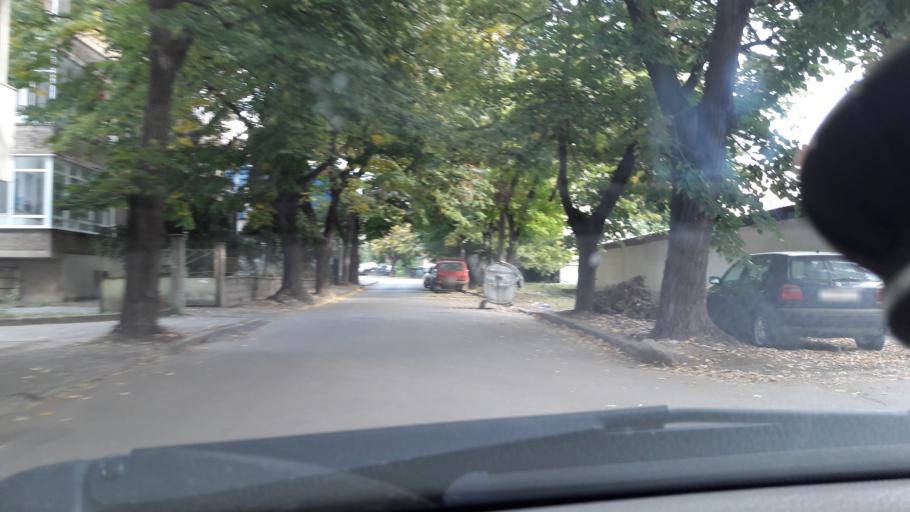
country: BG
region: Razgrad
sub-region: Obshtina Razgrad
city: Razgrad
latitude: 43.5288
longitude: 26.5258
